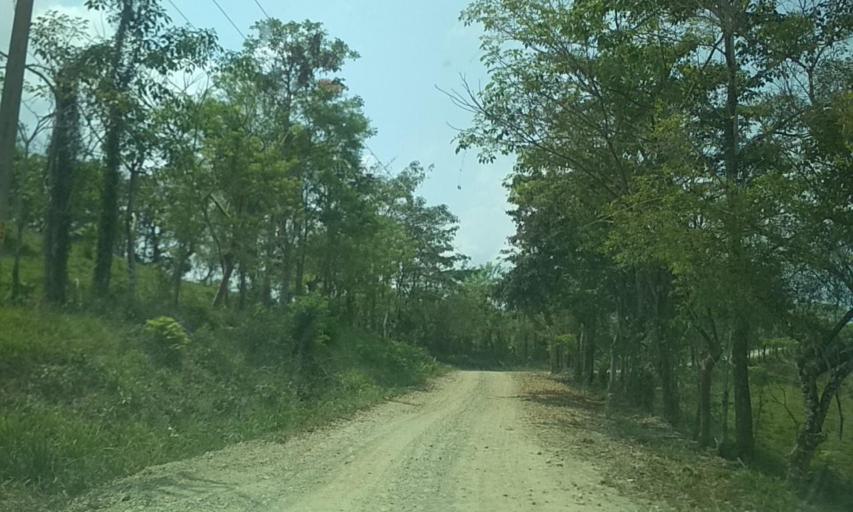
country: MX
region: Tabasco
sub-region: Huimanguillo
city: Francisco Rueda
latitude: 17.6307
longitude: -93.8211
